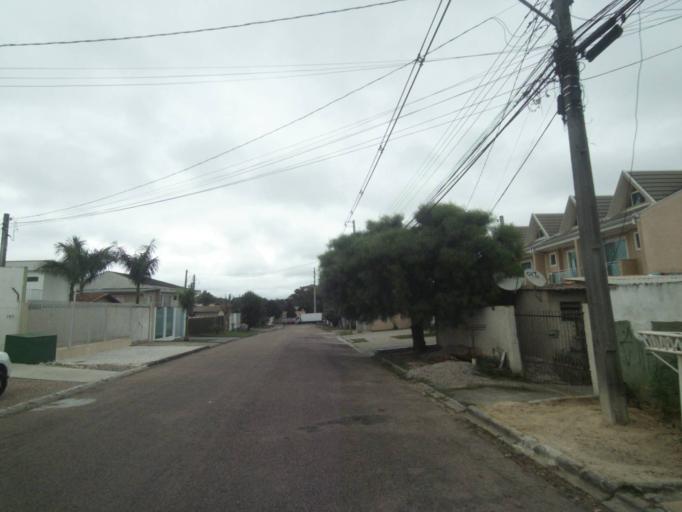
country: BR
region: Parana
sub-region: Sao Jose Dos Pinhais
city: Sao Jose dos Pinhais
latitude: -25.5423
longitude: -49.2781
